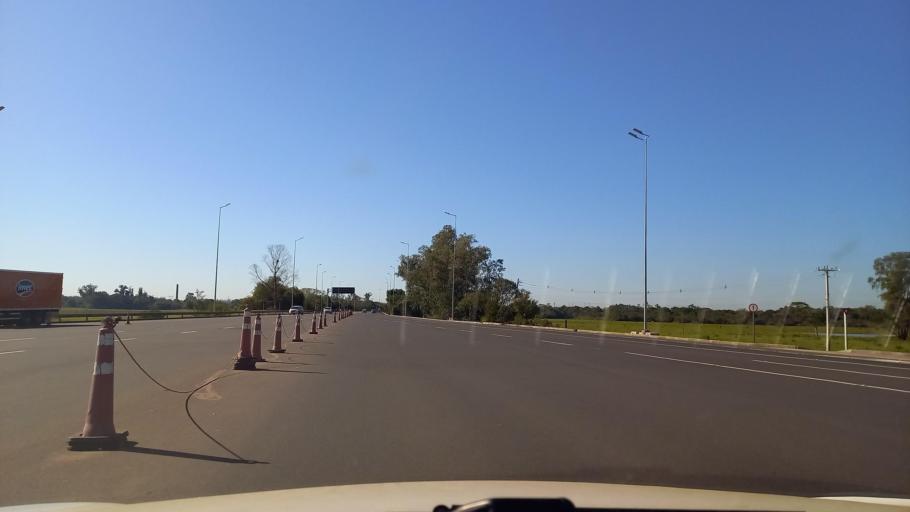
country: BR
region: Rio Grande do Sul
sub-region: Montenegro
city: Montenegro
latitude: -29.8198
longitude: -51.3607
